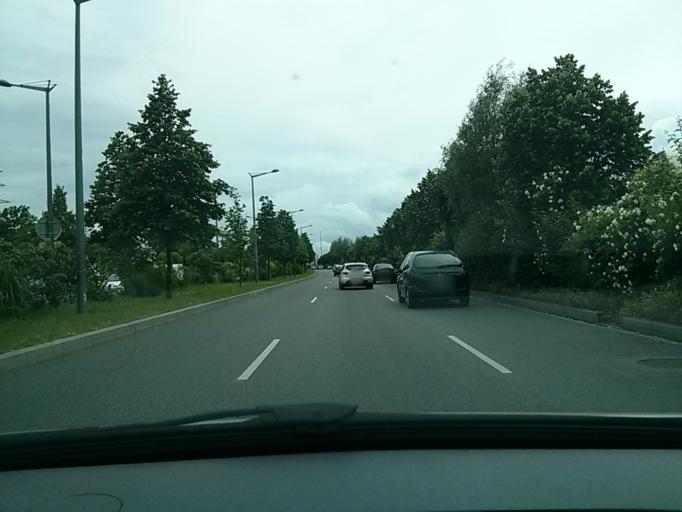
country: FR
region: Rhone-Alpes
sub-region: Departement du Rhone
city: Saint-Fons
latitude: 45.7214
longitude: 4.8421
